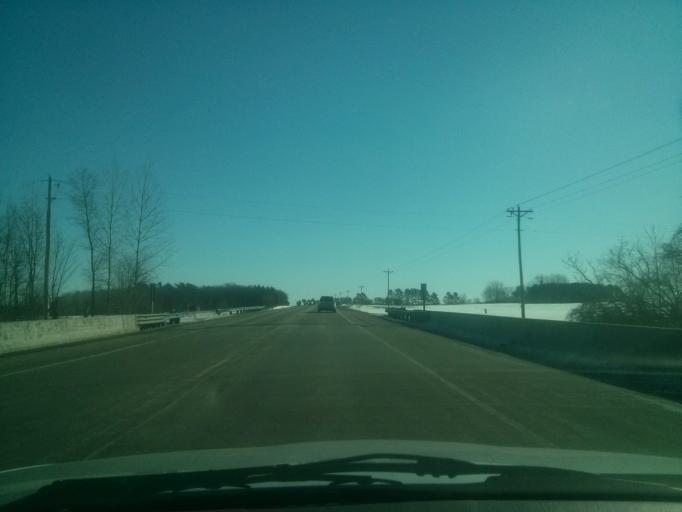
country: US
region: Wisconsin
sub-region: Saint Croix County
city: New Richmond
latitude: 45.1370
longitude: -92.4112
